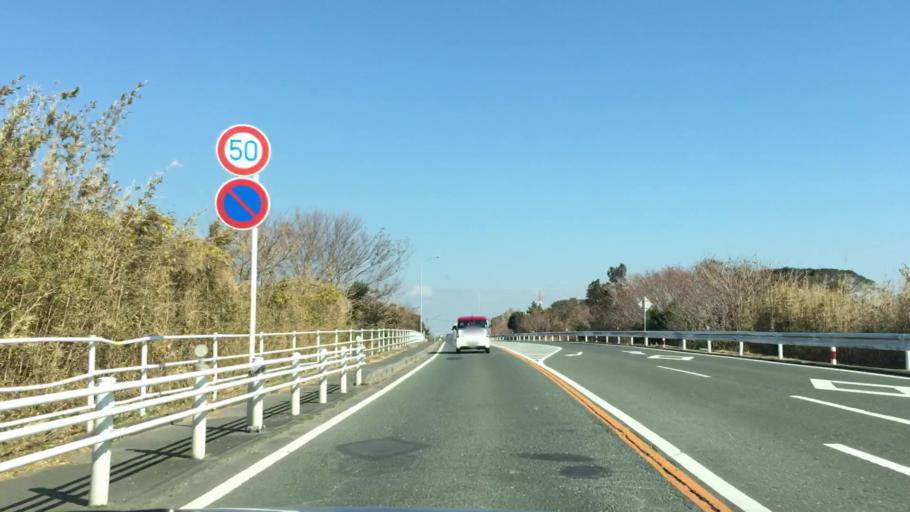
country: JP
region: Aichi
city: Tahara
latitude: 34.6670
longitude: 137.2858
